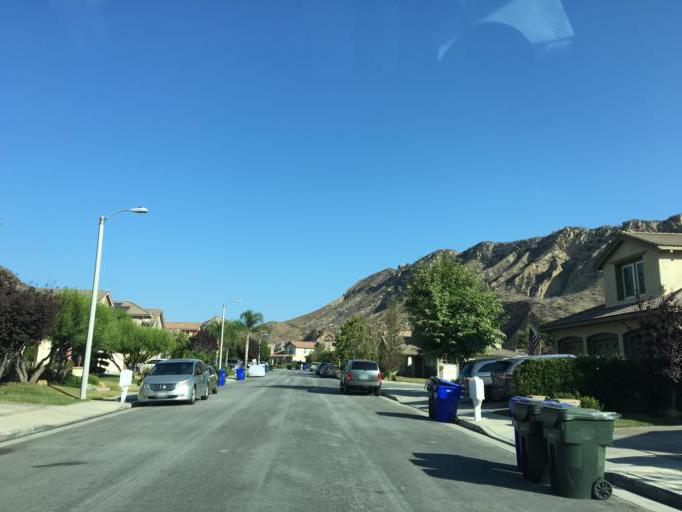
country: US
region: California
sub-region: Los Angeles County
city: Santa Clarita
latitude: 34.3762
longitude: -118.5917
